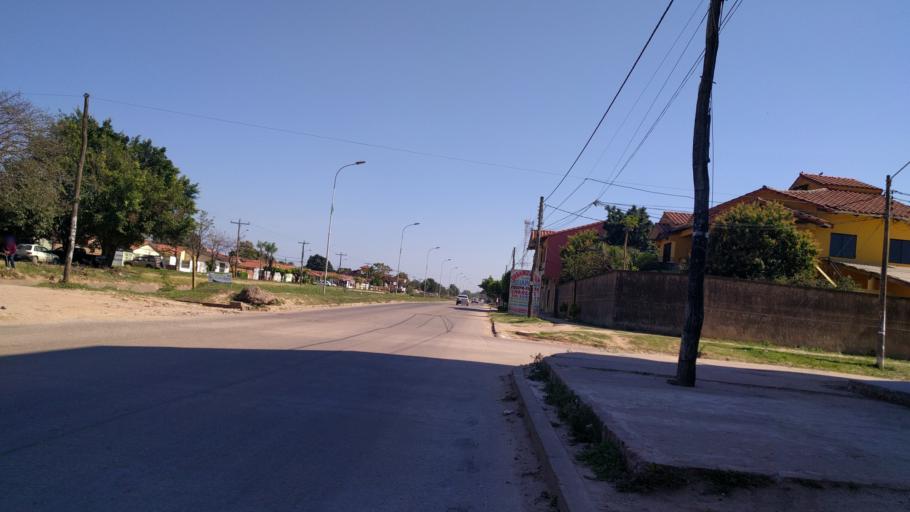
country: BO
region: Santa Cruz
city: Santa Cruz de la Sierra
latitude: -17.8562
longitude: -63.1910
